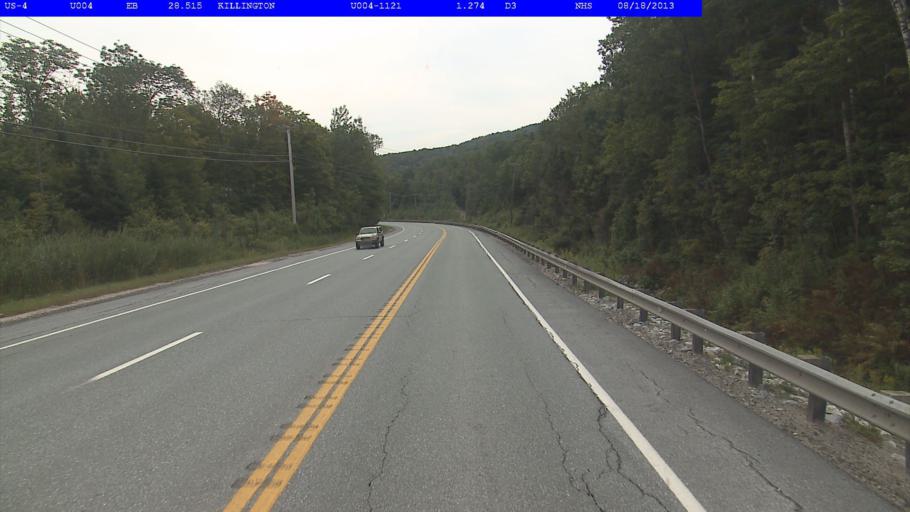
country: US
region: Vermont
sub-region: Rutland County
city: Rutland
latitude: 43.6639
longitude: -72.8220
